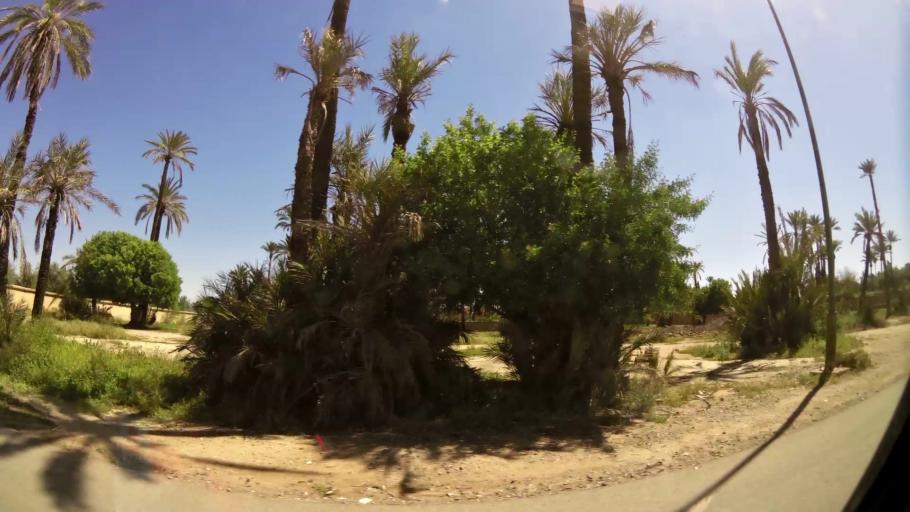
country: MA
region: Marrakech-Tensift-Al Haouz
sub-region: Marrakech
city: Marrakesh
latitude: 31.6742
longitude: -7.9853
